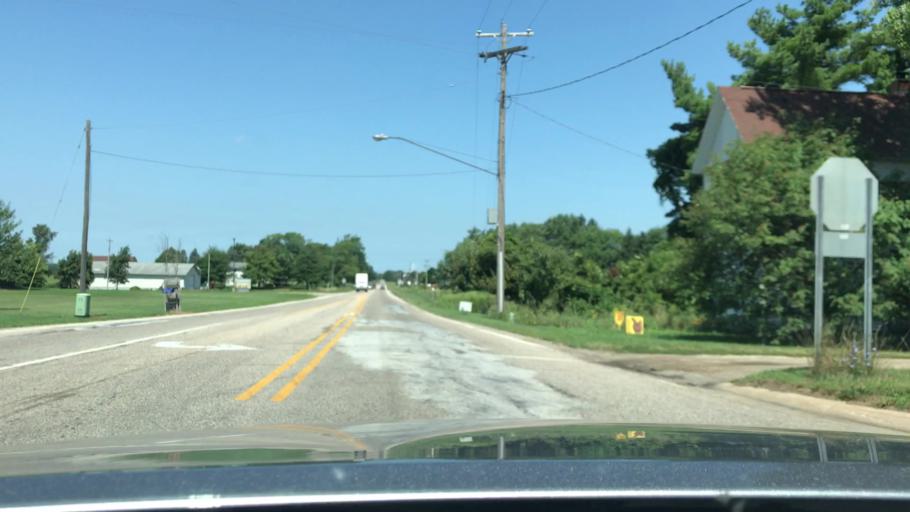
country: US
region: Michigan
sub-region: Ottawa County
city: Zeeland
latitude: 42.8854
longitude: -86.0803
